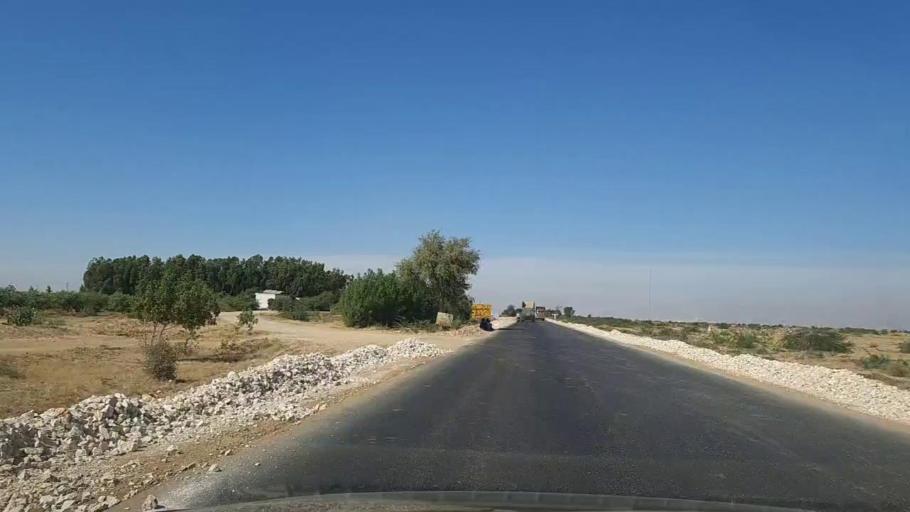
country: PK
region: Sindh
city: Kotri
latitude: 25.2626
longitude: 68.2215
